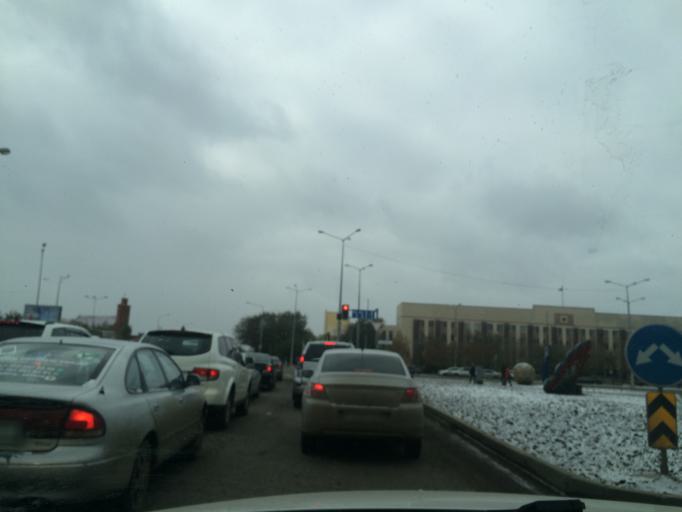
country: KZ
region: Astana Qalasy
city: Astana
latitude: 51.1557
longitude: 71.4544
